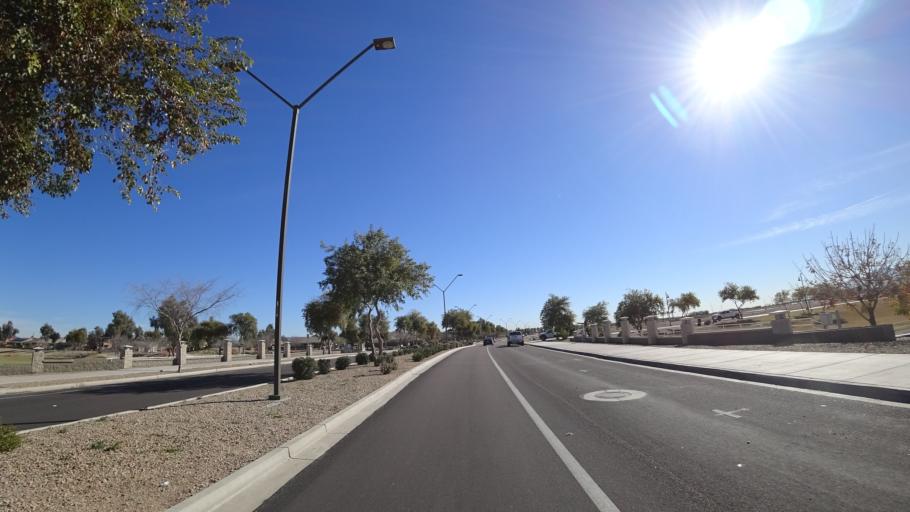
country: US
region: Arizona
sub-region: Maricopa County
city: Litchfield Park
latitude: 33.4752
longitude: -112.3867
